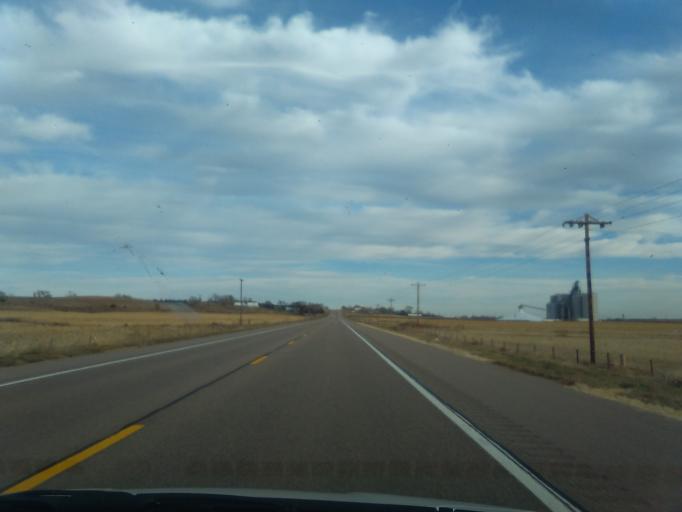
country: US
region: Nebraska
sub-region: Hitchcock County
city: Trenton
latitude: 40.2343
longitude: -100.8713
